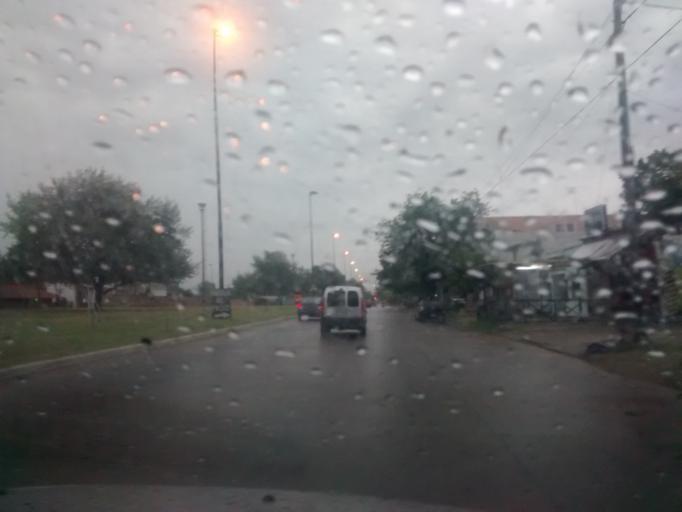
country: AR
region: Buenos Aires
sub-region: Partido de La Plata
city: La Plata
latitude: -34.9306
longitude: -57.9833
